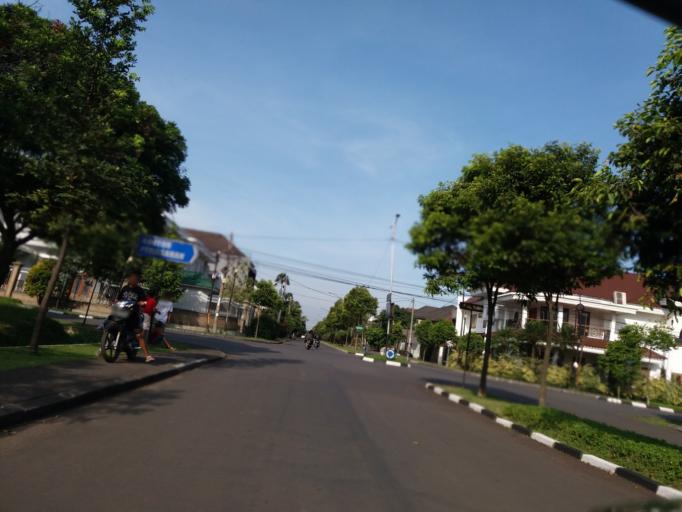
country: ID
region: West Java
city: Bandung
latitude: -6.9590
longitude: 107.6274
